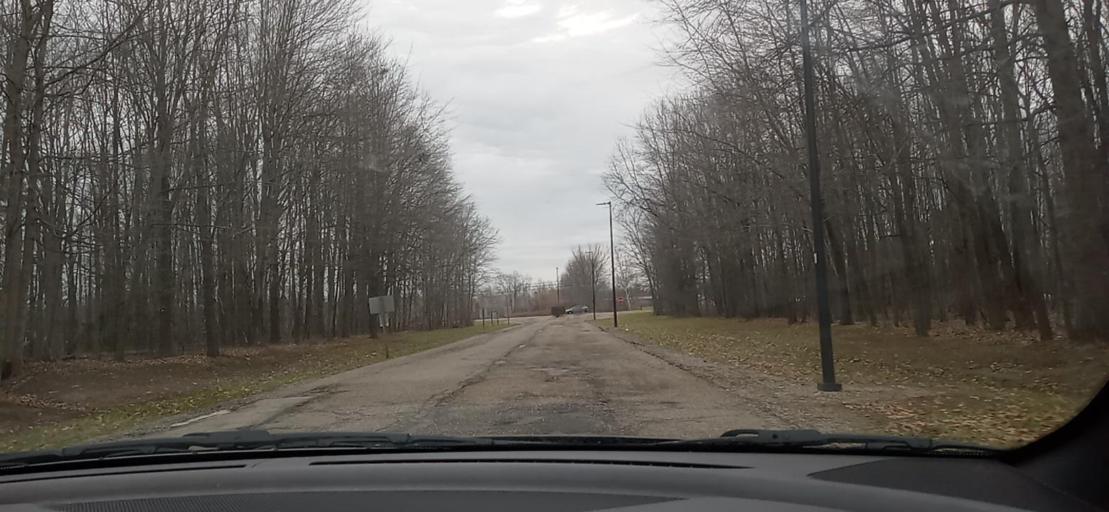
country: US
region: Ohio
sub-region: Trumbull County
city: Leavittsburg
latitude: 41.2342
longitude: -80.8893
